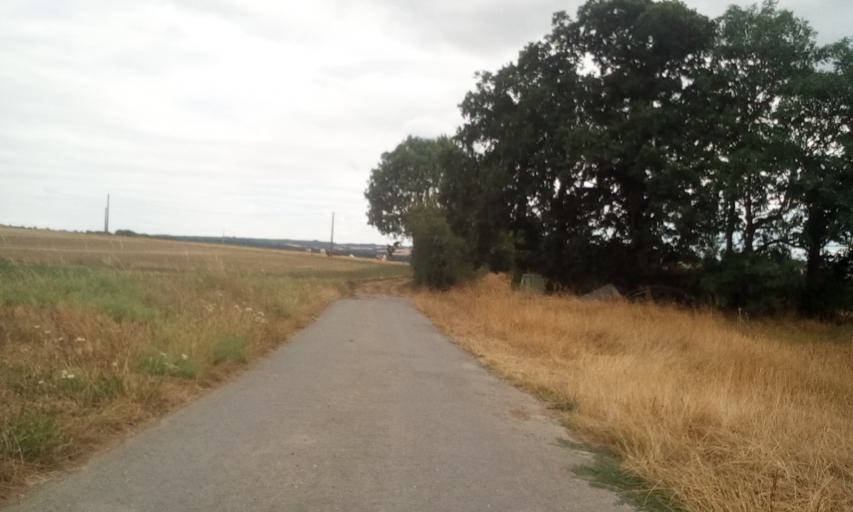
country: FR
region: Lower Normandy
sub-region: Departement du Calvados
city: Thury-Harcourt
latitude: 48.9825
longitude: -0.4401
